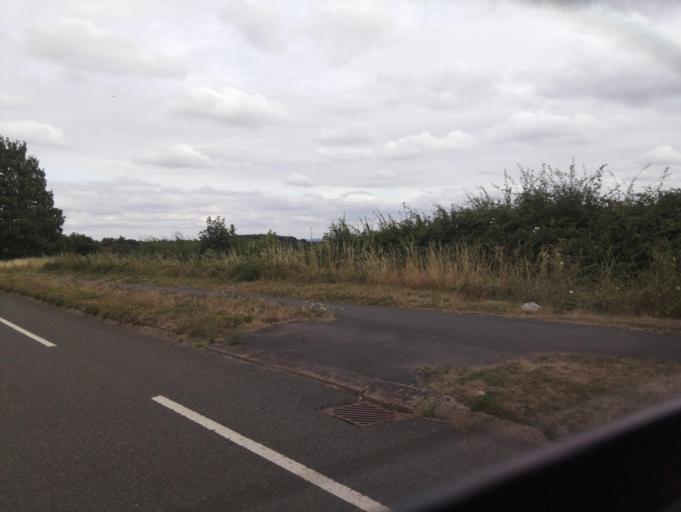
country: GB
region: England
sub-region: Derbyshire
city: Borrowash
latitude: 52.9168
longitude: -1.3300
